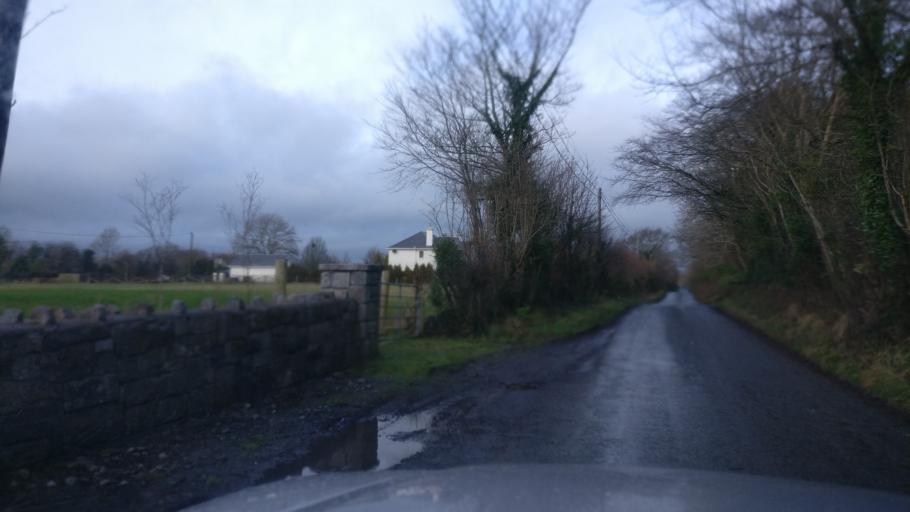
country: IE
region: Connaught
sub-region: County Galway
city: Athenry
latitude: 53.2510
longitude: -8.7200
